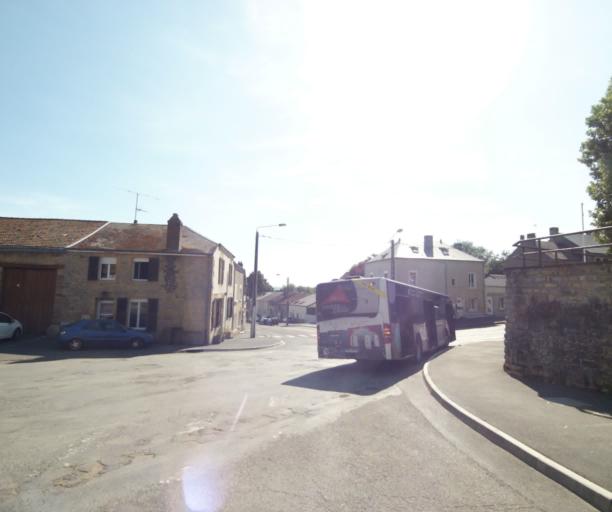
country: FR
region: Champagne-Ardenne
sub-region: Departement des Ardennes
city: Warcq
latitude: 49.7881
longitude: 4.6947
